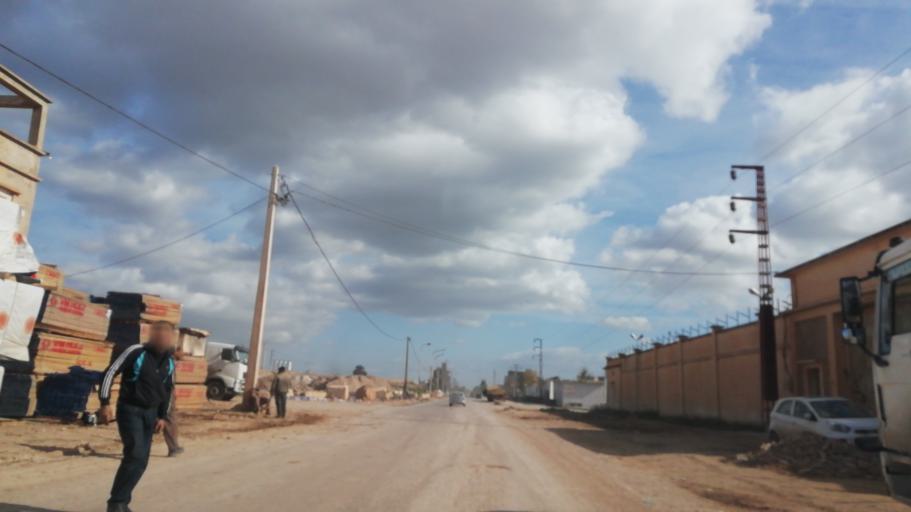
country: DZ
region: Oran
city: Es Senia
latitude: 35.6515
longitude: -0.5823
